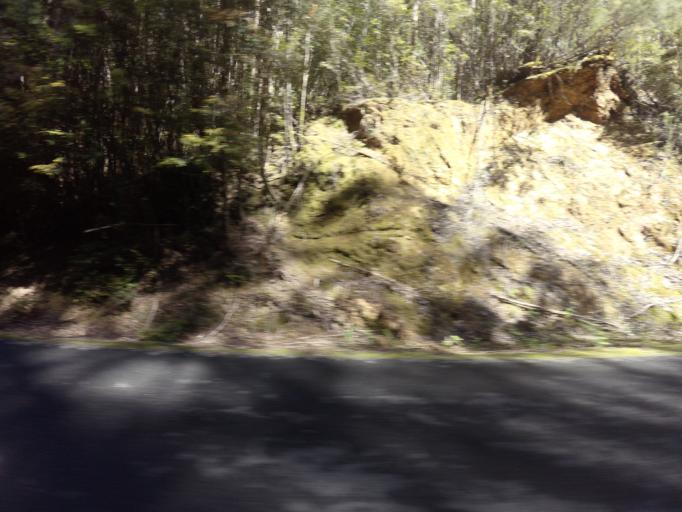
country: AU
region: Tasmania
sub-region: Huon Valley
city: Geeveston
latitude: -42.8204
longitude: 146.2948
